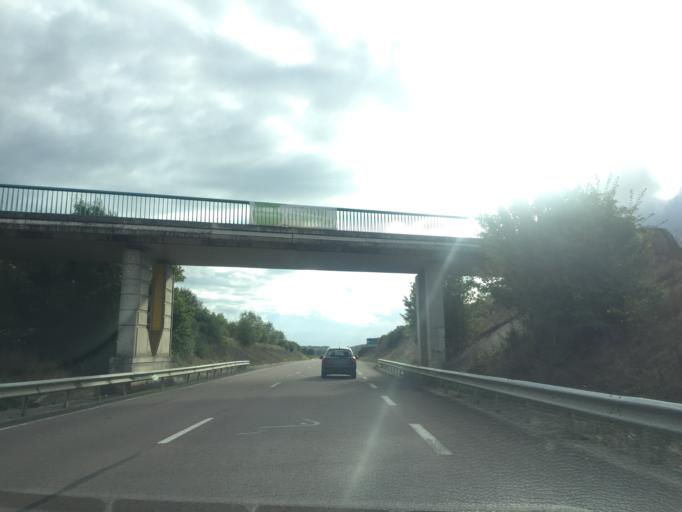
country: FR
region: Lorraine
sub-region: Departement des Vosges
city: Chatenois
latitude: 48.2970
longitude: 5.9072
